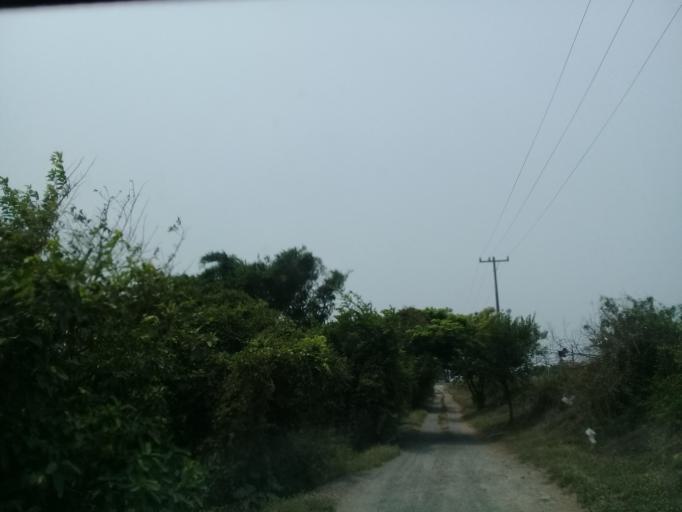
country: MX
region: Veracruz
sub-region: Veracruz
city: Hacienda Sotavento
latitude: 19.1420
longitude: -96.1590
